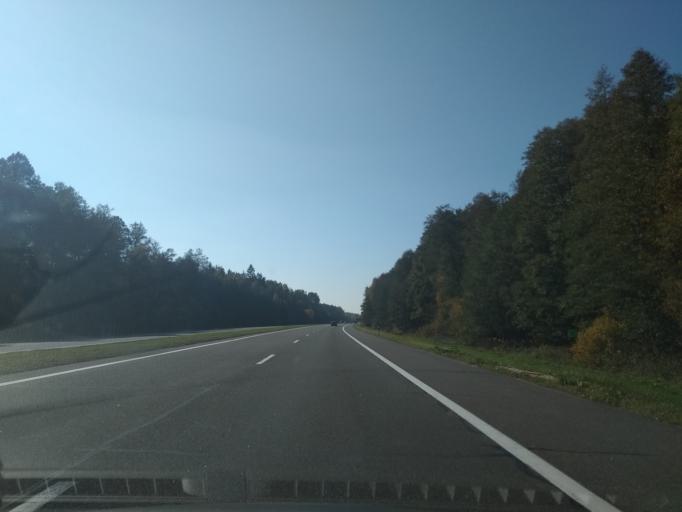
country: BY
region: Brest
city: Ivatsevichy
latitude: 52.8494
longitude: 25.6370
